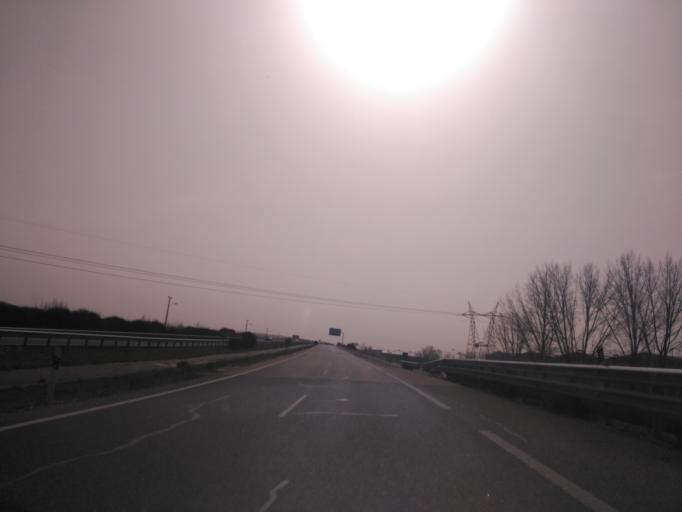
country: ES
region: Castille and Leon
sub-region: Provincia de Palencia
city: Villamuriel de Cerrato
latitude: 41.9654
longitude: -4.5047
